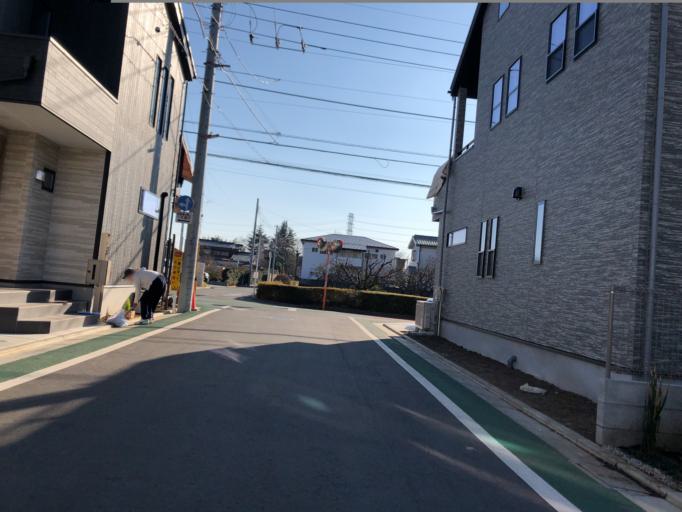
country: JP
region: Tokyo
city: Mitaka-shi
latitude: 35.6851
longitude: 139.5440
